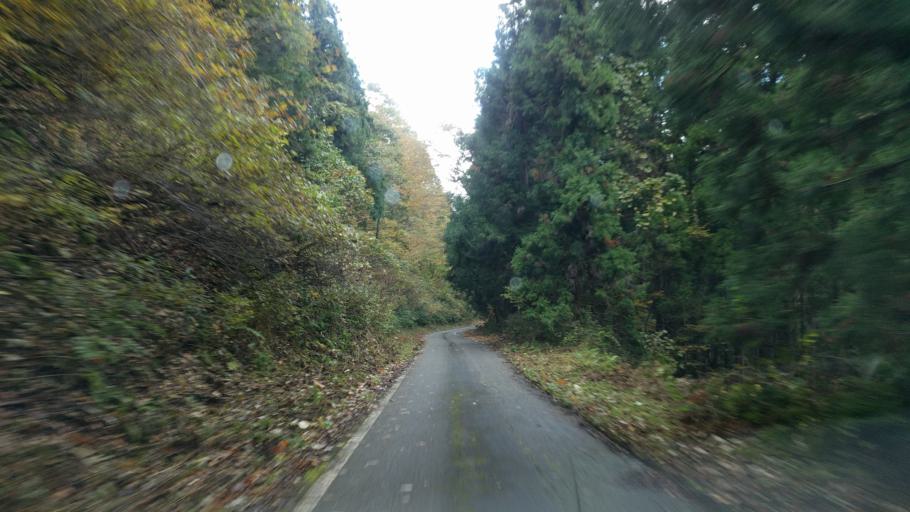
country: JP
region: Fukushima
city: Kitakata
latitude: 37.4070
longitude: 139.7054
